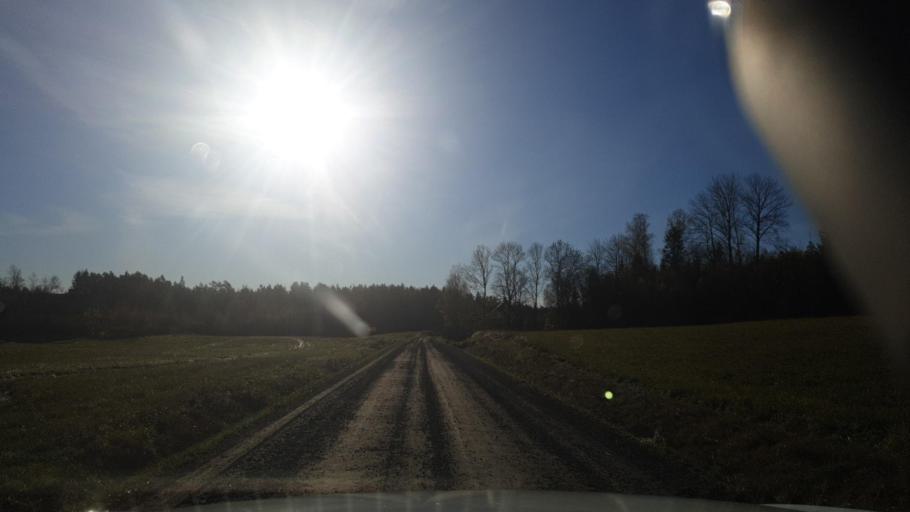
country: SE
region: Vaermland
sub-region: Karlstads Kommun
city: Edsvalla
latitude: 59.5049
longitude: 13.0295
